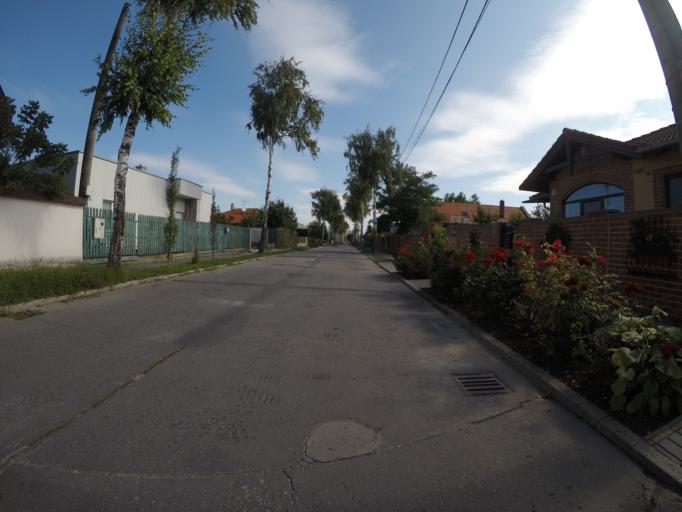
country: SK
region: Trnavsky
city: Dunajska Streda
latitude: 47.9878
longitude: 17.6219
